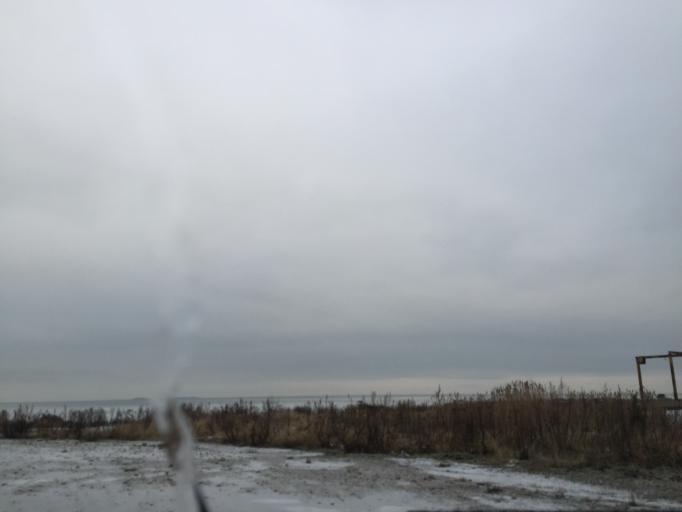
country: EE
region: Saare
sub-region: Orissaare vald
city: Orissaare
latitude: 58.6833
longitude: 23.1939
